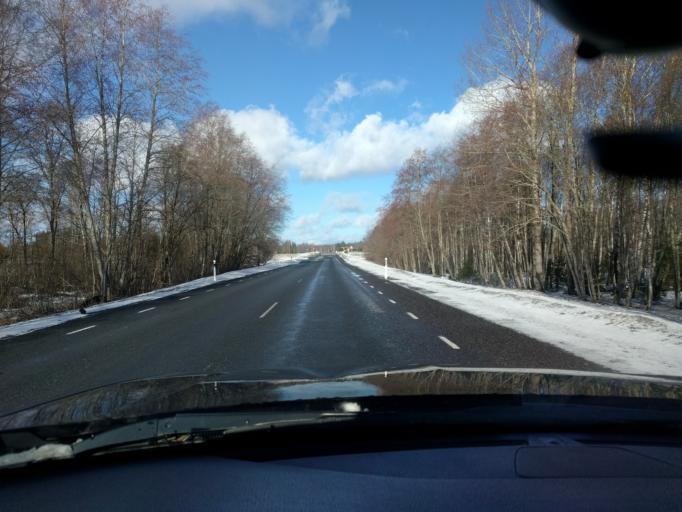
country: EE
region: Harju
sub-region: Anija vald
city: Kehra
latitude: 59.2292
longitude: 25.3911
